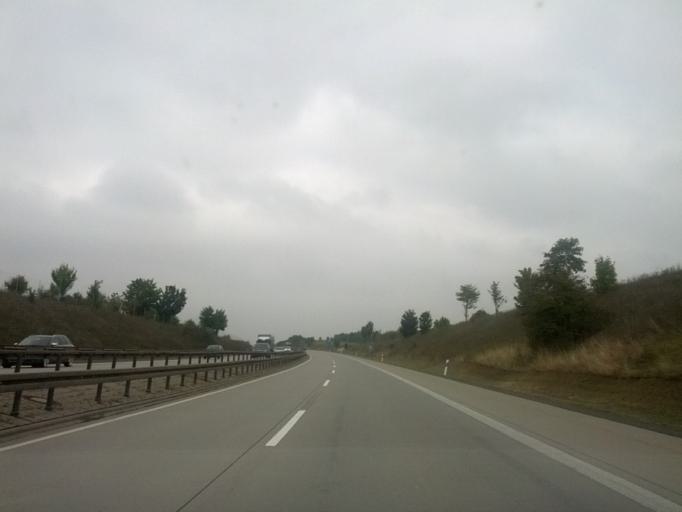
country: DE
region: Thuringia
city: Ingersleben
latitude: 50.9289
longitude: 10.9541
